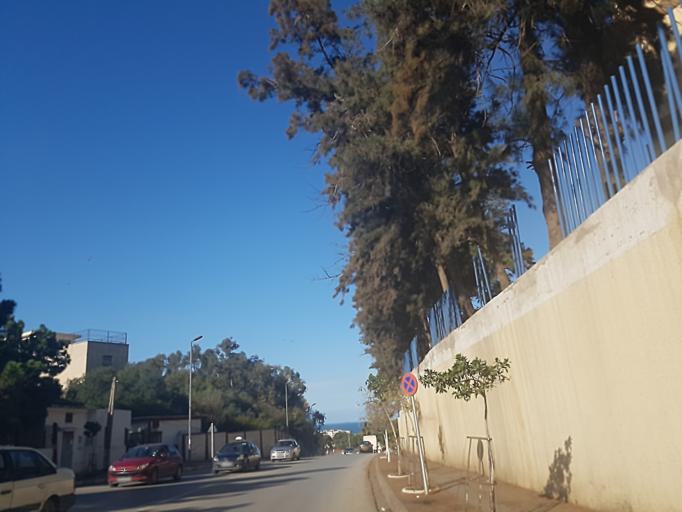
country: DZ
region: Alger
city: Birkhadem
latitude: 36.7343
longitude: 3.1046
